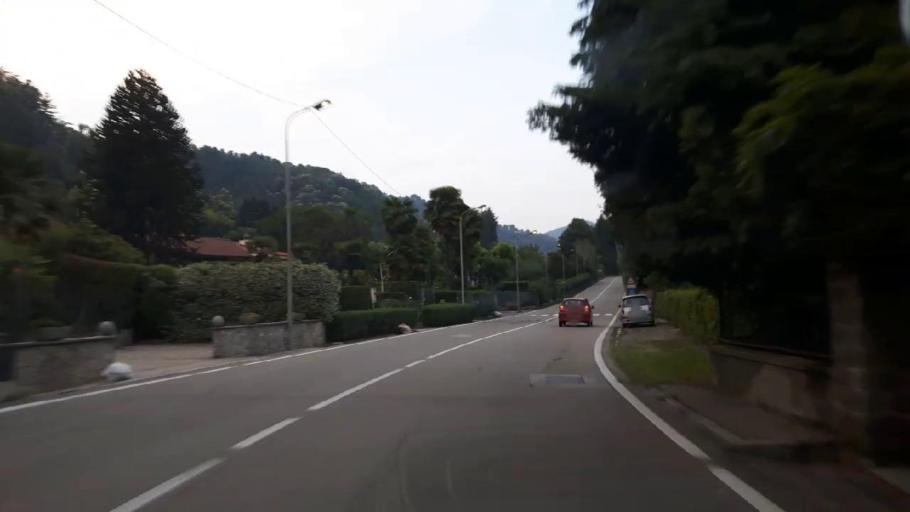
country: IT
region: Piedmont
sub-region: Provincia di Novara
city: Meina
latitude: 45.7989
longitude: 8.5373
